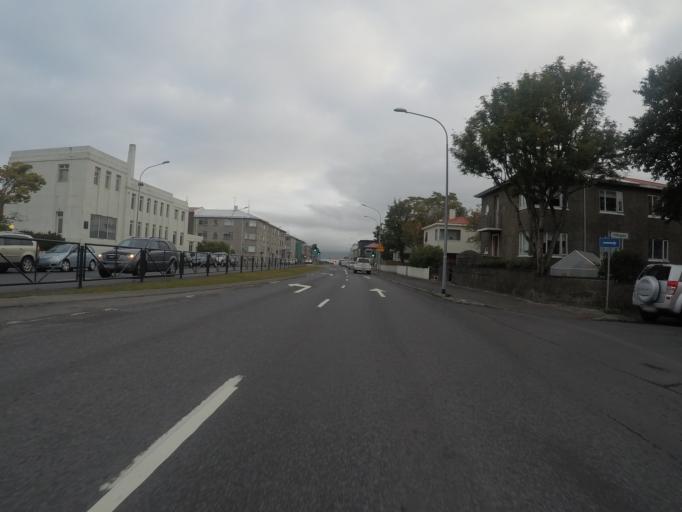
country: IS
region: Capital Region
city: Reykjavik
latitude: 64.1409
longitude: -21.9188
